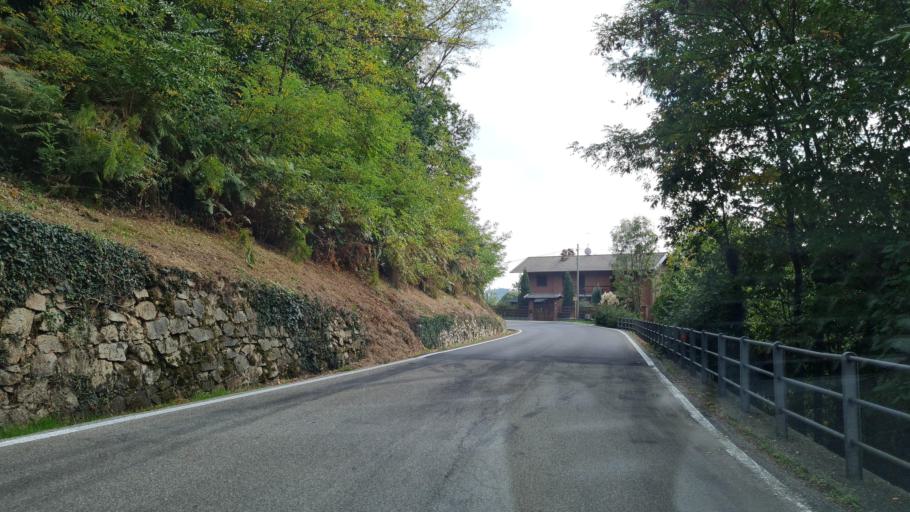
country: IT
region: Piedmont
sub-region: Provincia di Biella
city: Mezzana Mortigliengo
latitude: 45.6273
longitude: 8.1857
